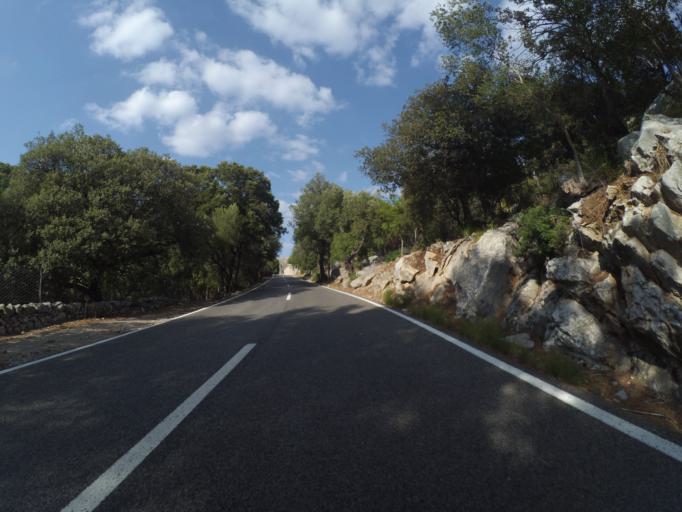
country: ES
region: Balearic Islands
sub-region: Illes Balears
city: Selva
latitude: 39.7902
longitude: 2.8943
